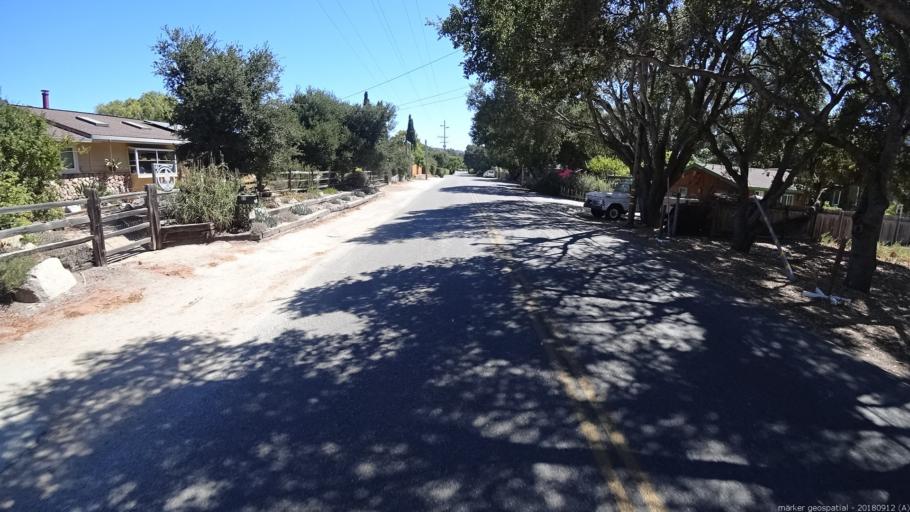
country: US
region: California
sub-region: Monterey County
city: Carmel Valley Village
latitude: 36.4812
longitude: -121.7303
